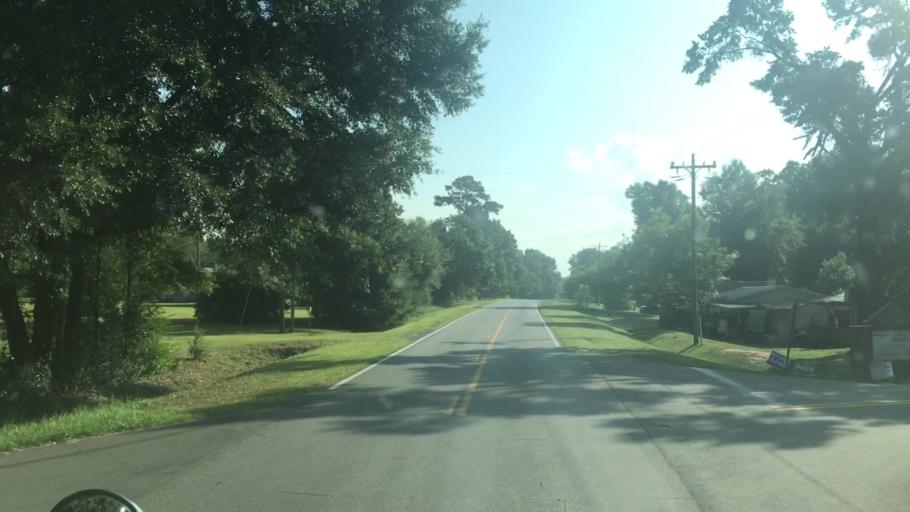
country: US
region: Florida
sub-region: Gadsden County
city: Quincy
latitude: 30.6581
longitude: -84.5641
